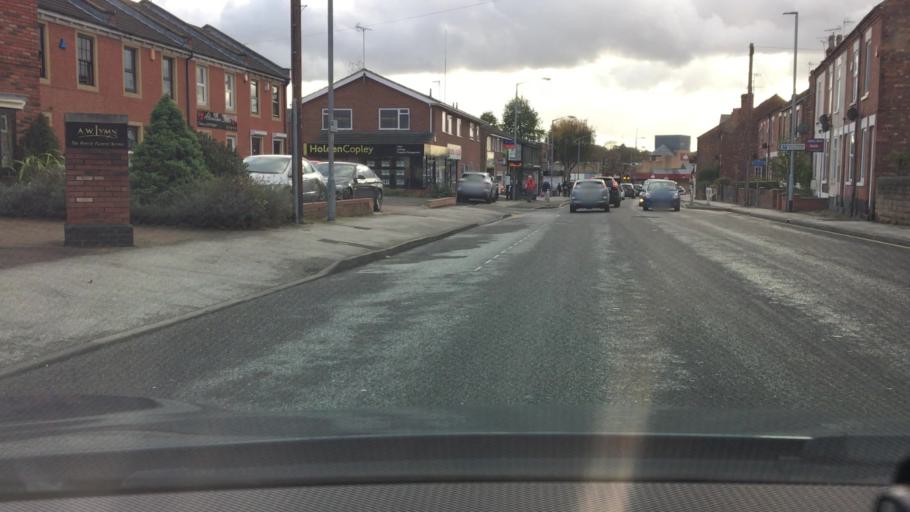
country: GB
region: England
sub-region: Nottinghamshire
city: Arnold
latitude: 53.0034
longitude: -1.1293
